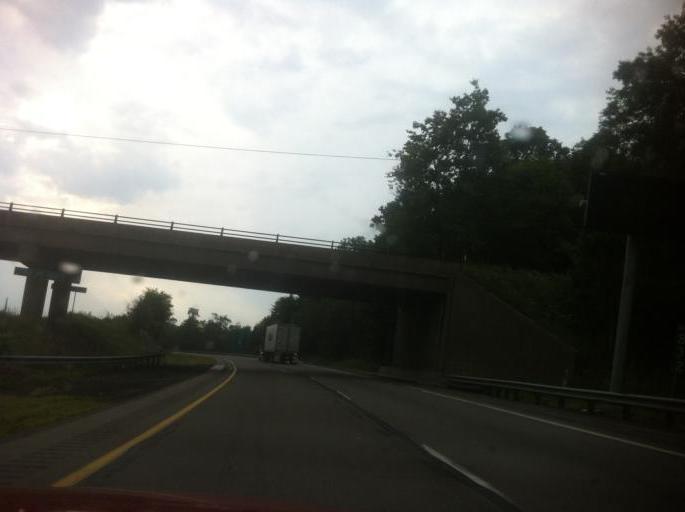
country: US
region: Pennsylvania
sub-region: Jefferson County
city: Brookville
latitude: 41.1692
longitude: -79.0116
